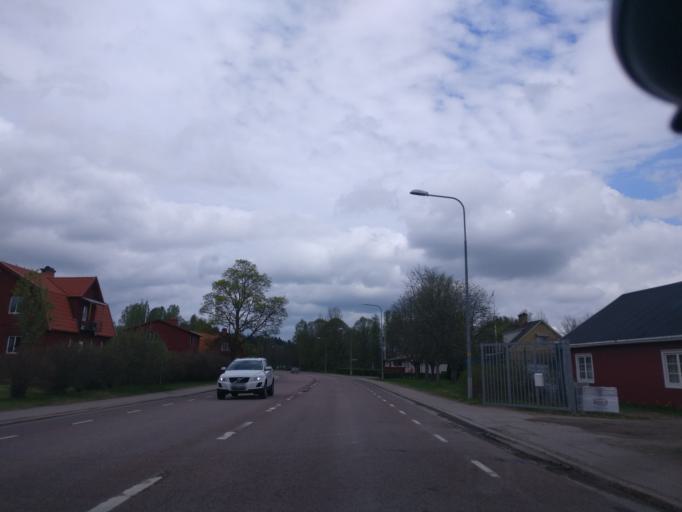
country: SE
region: Vaermland
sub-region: Hagfors Kommun
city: Ekshaerad
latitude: 60.1784
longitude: 13.4962
